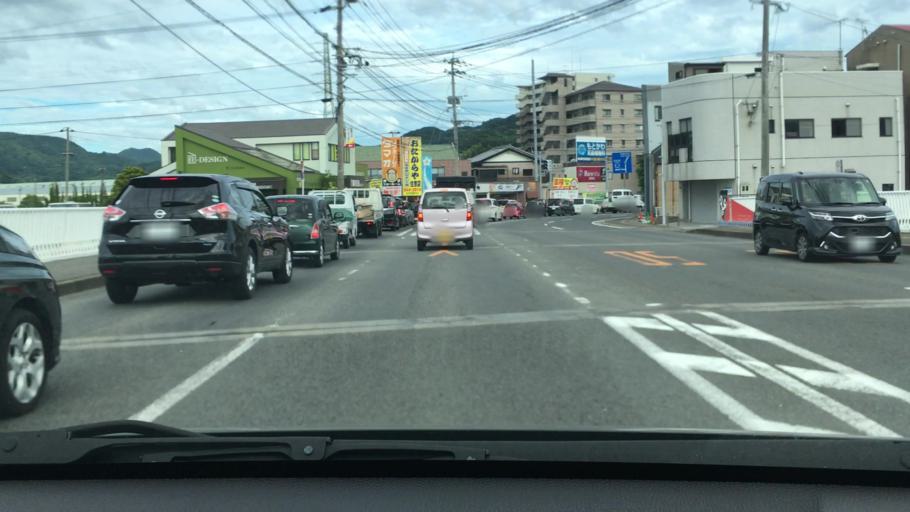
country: JP
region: Nagasaki
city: Togitsu
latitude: 32.8317
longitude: 129.8463
